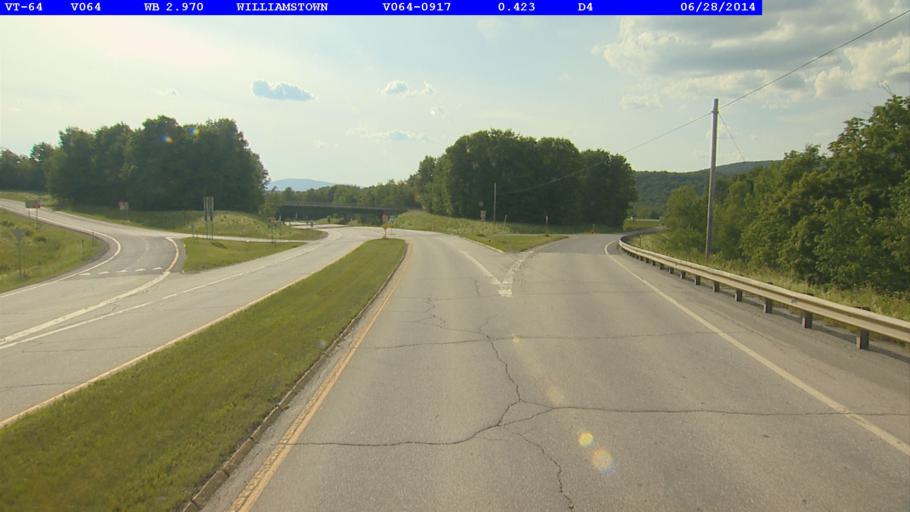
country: US
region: Vermont
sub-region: Washington County
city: Northfield
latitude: 44.1144
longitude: -72.6050
